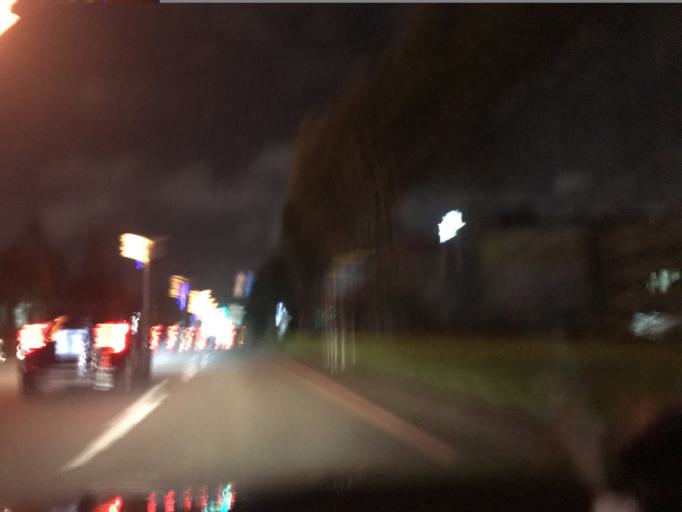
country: TW
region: Taiwan
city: Taoyuan City
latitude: 24.9798
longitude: 121.2362
